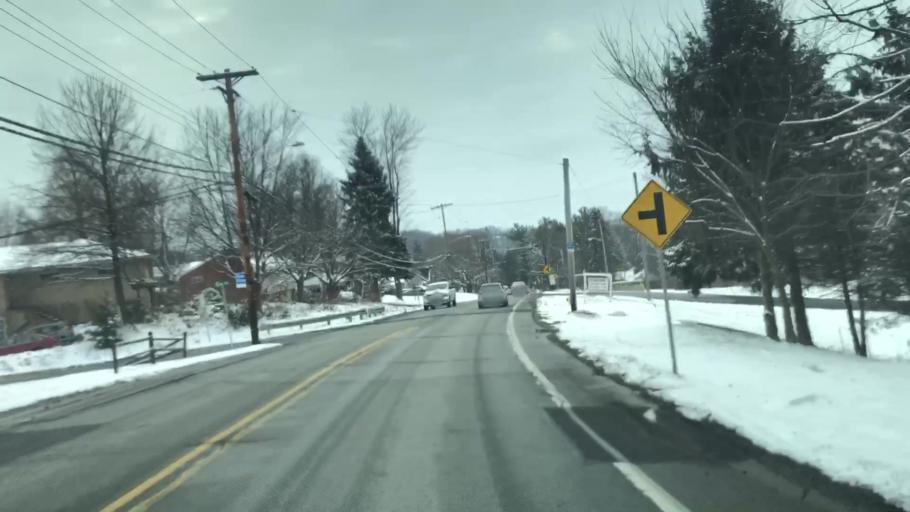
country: US
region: Pennsylvania
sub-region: Allegheny County
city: Monroeville
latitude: 40.4541
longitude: -79.7605
